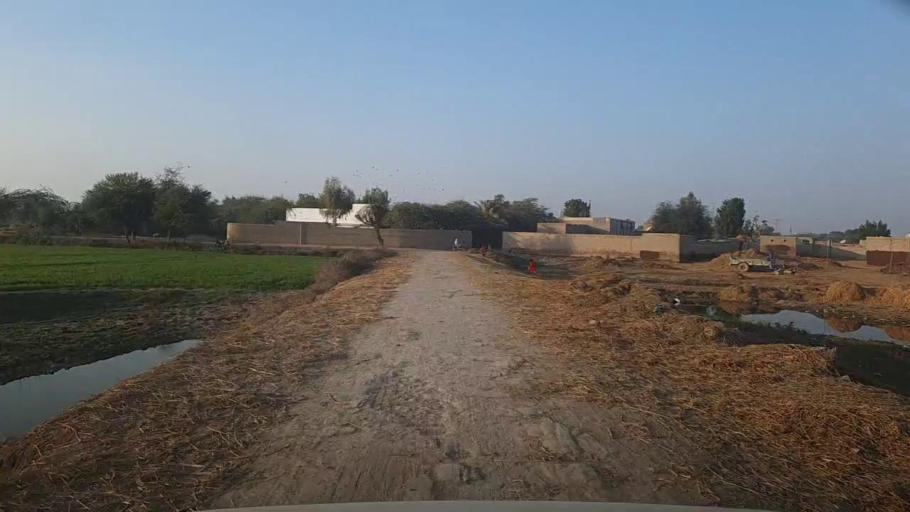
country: PK
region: Sindh
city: Mehar
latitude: 27.1979
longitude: 67.7812
